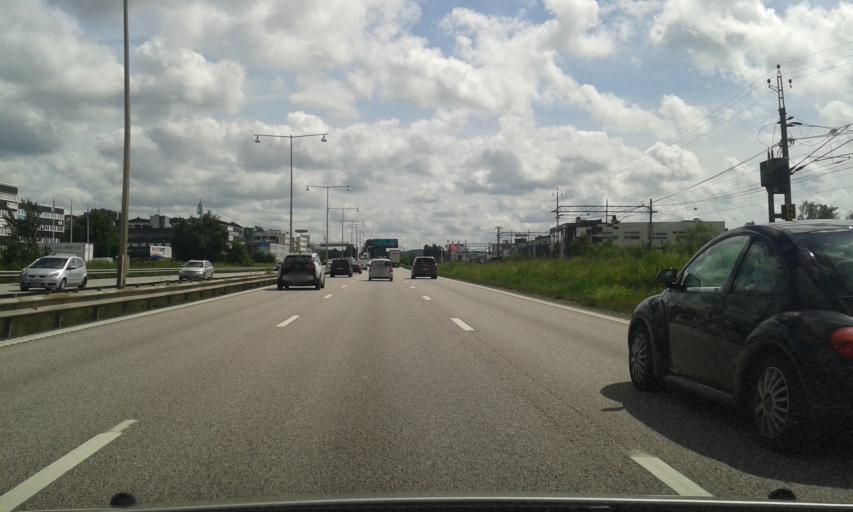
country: SE
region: Vaestra Goetaland
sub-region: Molndal
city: Moelndal
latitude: 57.6714
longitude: 12.0127
